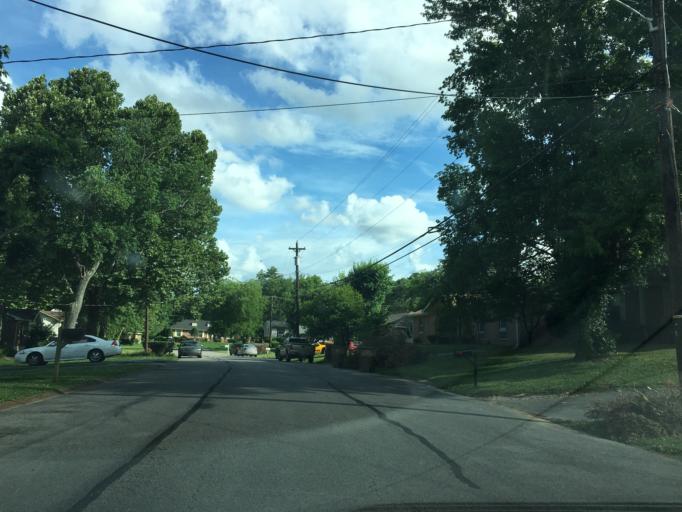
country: US
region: Tennessee
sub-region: Davidson County
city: Oak Hill
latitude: 36.0824
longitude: -86.7174
